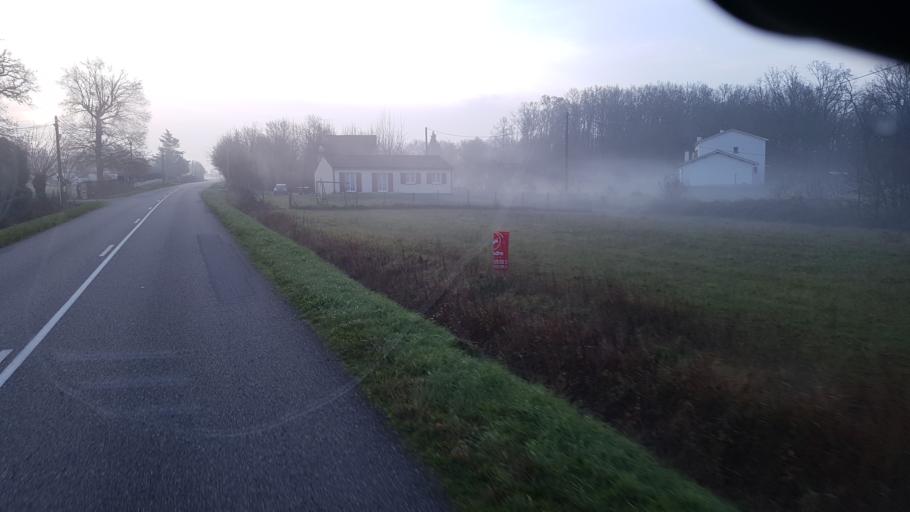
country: FR
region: Midi-Pyrenees
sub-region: Departement du Tarn-et-Garonne
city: Caussade
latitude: 44.1468
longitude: 1.5570
